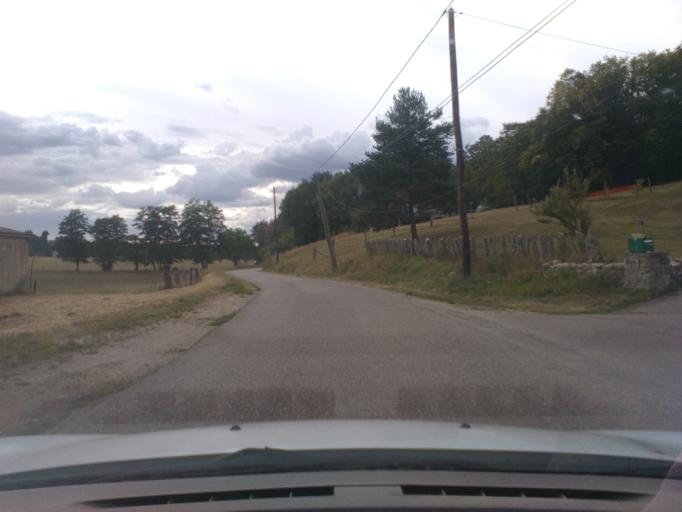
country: FR
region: Lorraine
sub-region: Departement des Vosges
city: Nomexy
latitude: 48.3274
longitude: 6.3695
